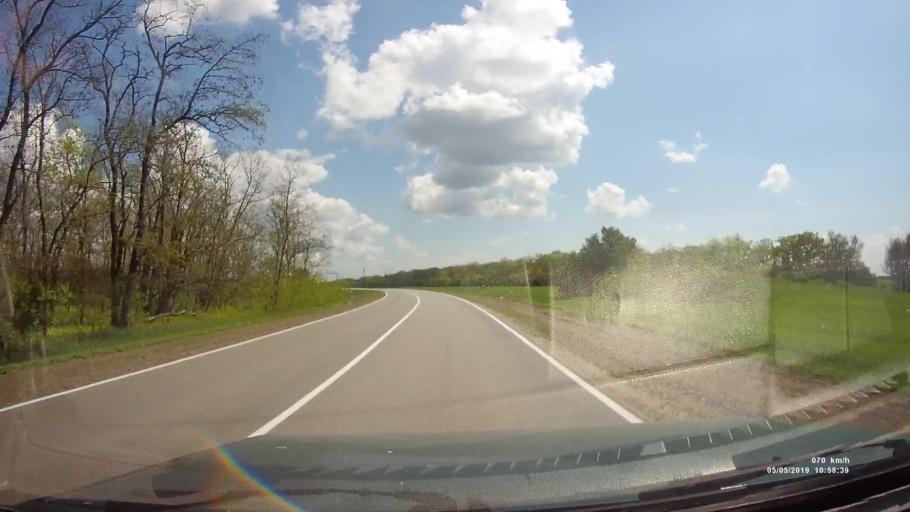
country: RU
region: Rostov
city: Ust'-Donetskiy
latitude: 47.6688
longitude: 40.8564
